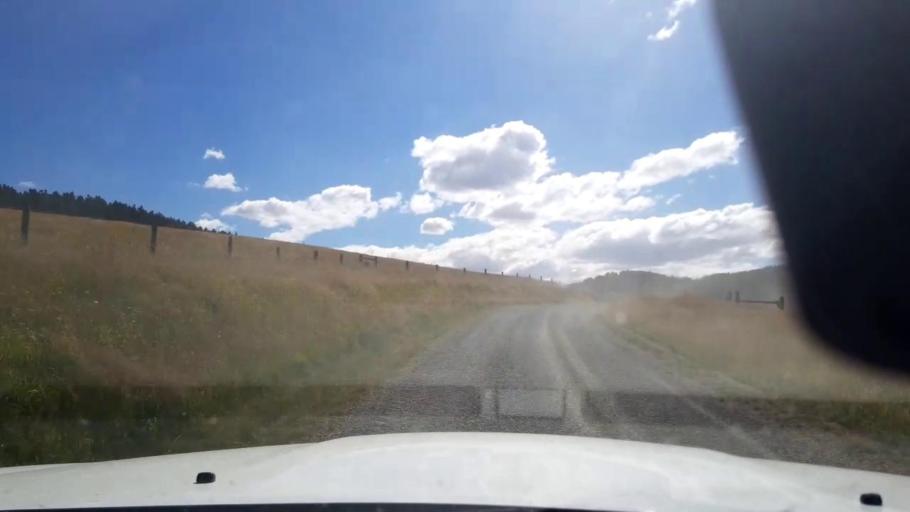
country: NZ
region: Canterbury
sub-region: Timaru District
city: Pleasant Point
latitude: -44.3123
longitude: 170.9164
